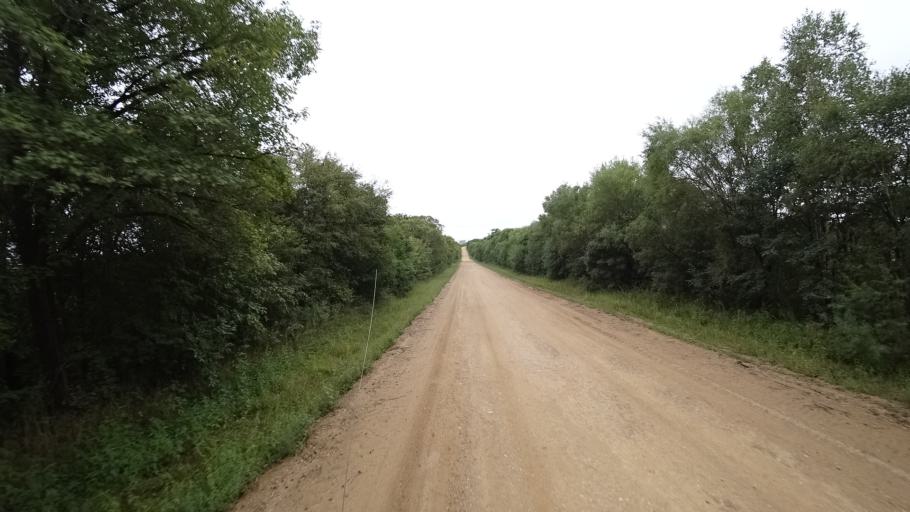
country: RU
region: Primorskiy
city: Monastyrishche
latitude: 44.0877
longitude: 132.5972
